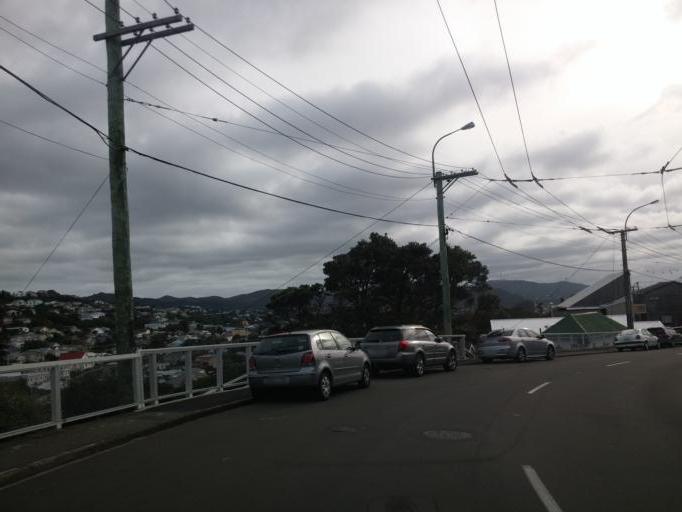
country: NZ
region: Wellington
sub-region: Wellington City
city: Brooklyn
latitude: -41.3087
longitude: 174.7661
